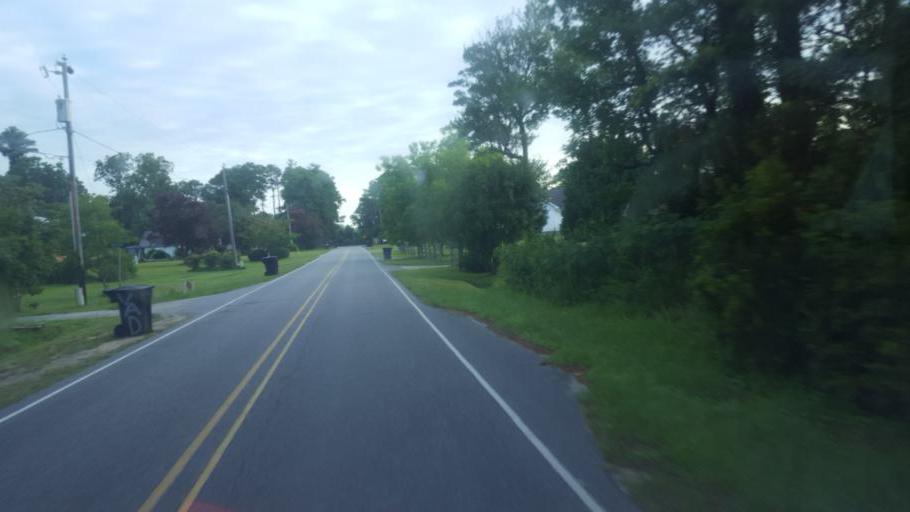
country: US
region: North Carolina
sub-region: Dare County
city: Wanchese
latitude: 35.8468
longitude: -75.6421
